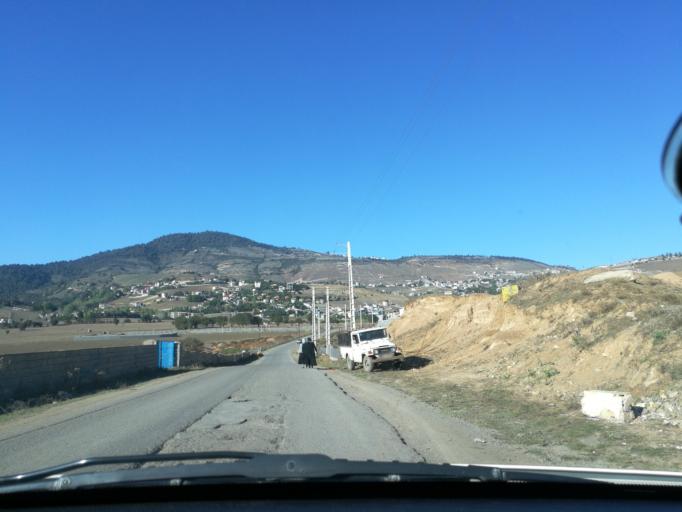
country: IR
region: Mazandaran
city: `Abbasabad
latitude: 36.5408
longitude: 51.1819
